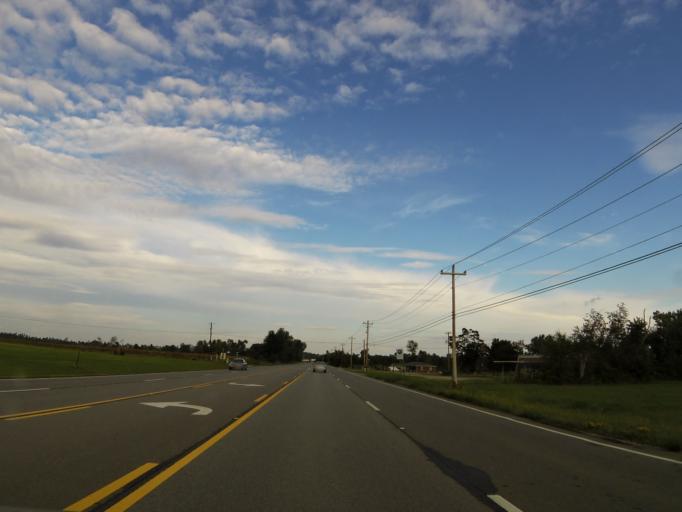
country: US
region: Alabama
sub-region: Lauderdale County
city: Rogersville
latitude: 34.7981
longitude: -87.1351
